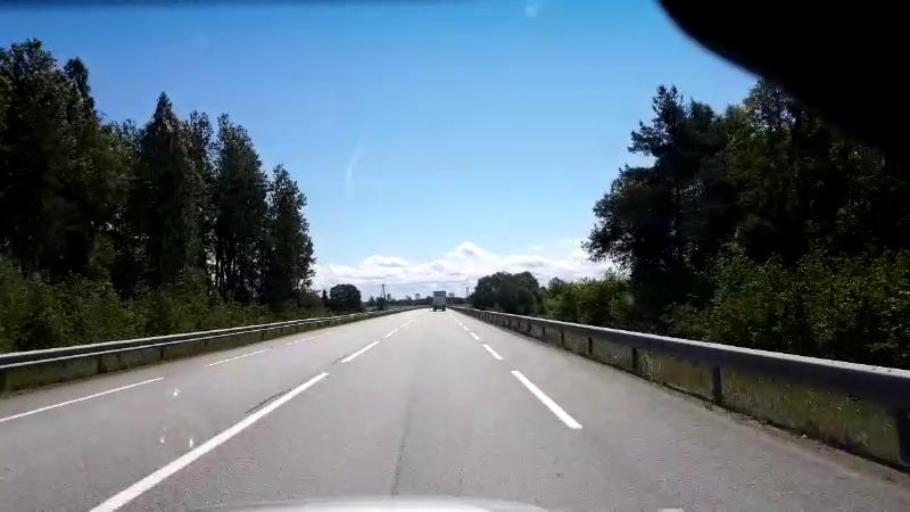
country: LV
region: Saulkrastu
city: Saulkrasti
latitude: 57.3390
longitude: 24.4497
